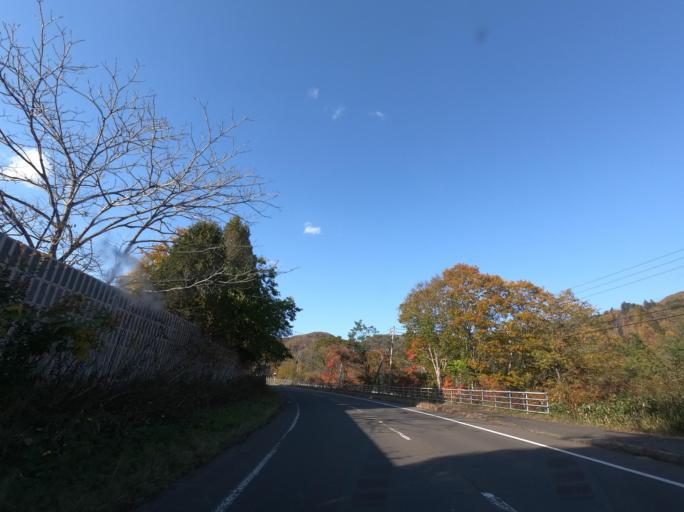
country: JP
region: Hokkaido
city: Iwamizawa
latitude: 43.0059
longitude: 142.0061
